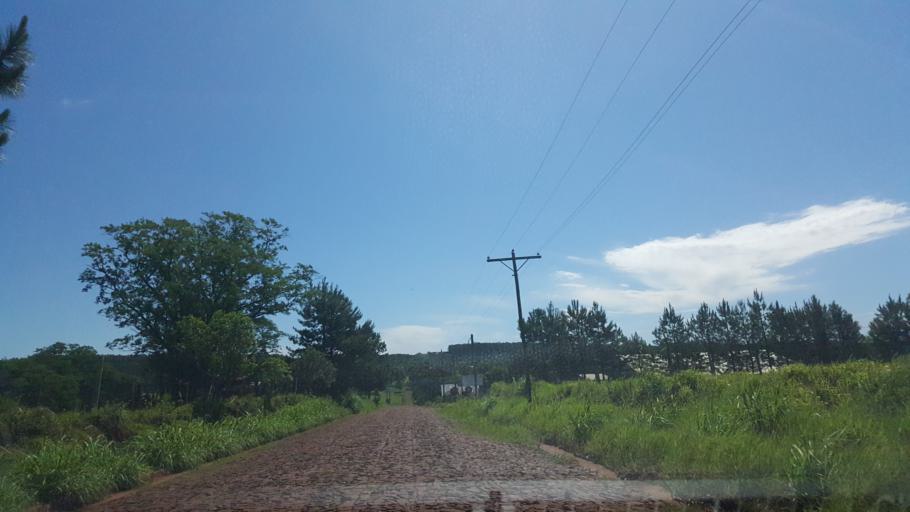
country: AR
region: Misiones
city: Capiovi
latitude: -26.9318
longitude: -55.0696
